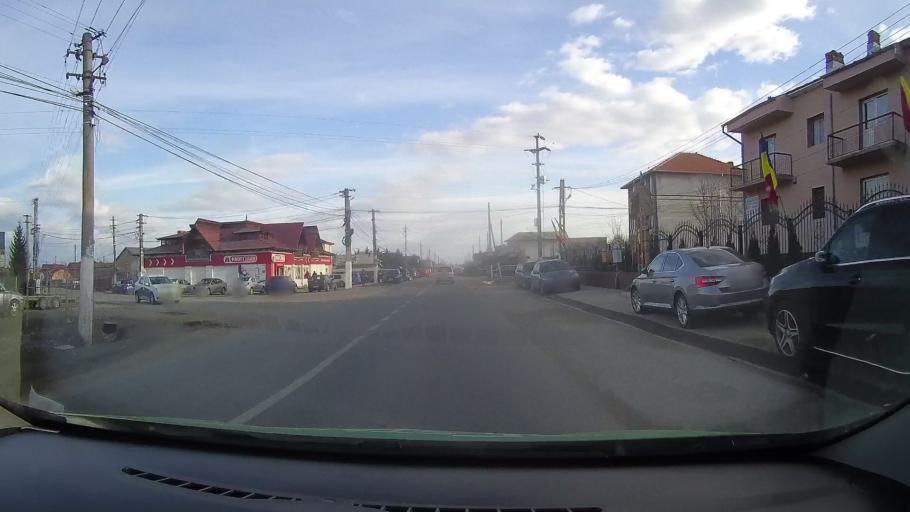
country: RO
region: Dambovita
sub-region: Comuna Vacaresti
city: Vacaresti
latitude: 44.8569
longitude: 25.4846
